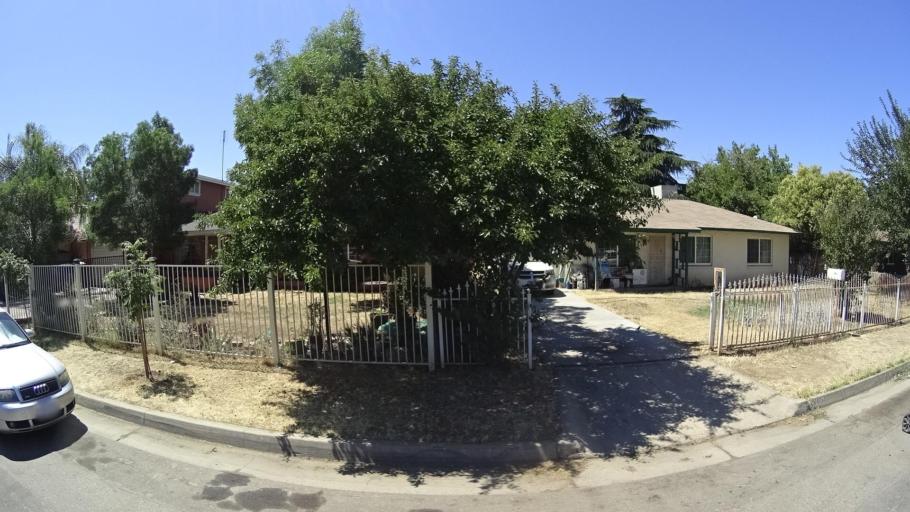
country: US
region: California
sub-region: Fresno County
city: Fresno
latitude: 36.7959
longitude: -119.7870
